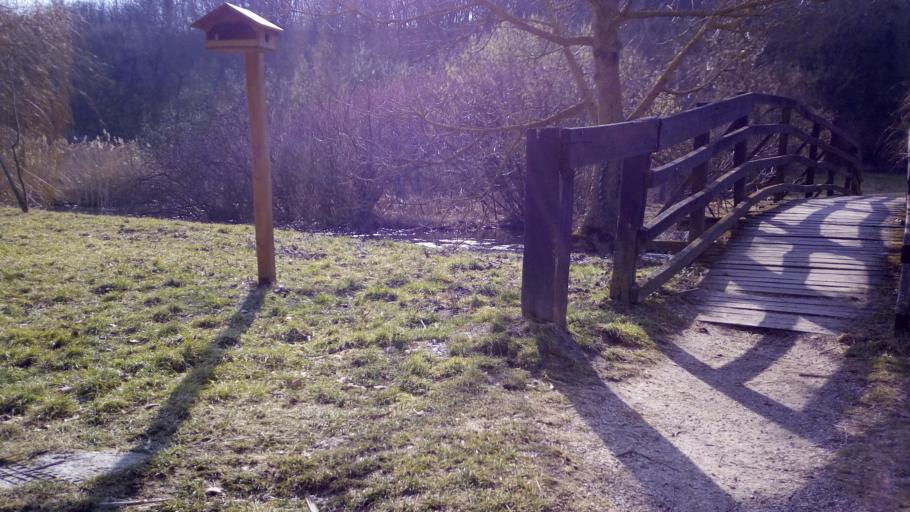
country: HU
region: Baranya
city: Pellerd
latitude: 46.0049
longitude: 18.2045
